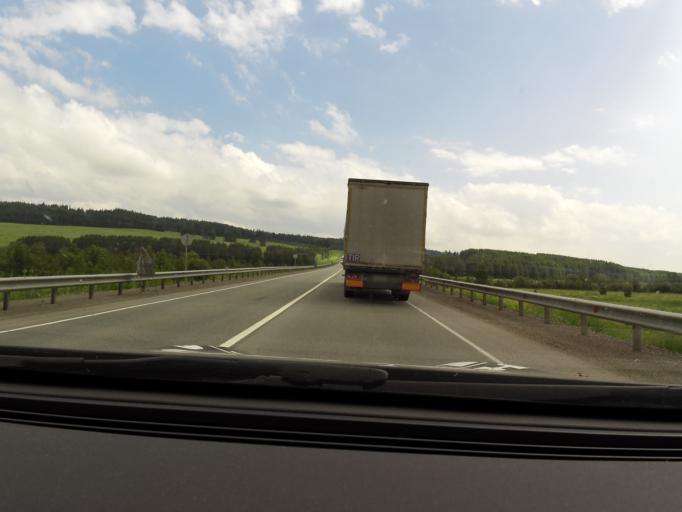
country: RU
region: Perm
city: Suksun
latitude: 57.0494
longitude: 57.4296
